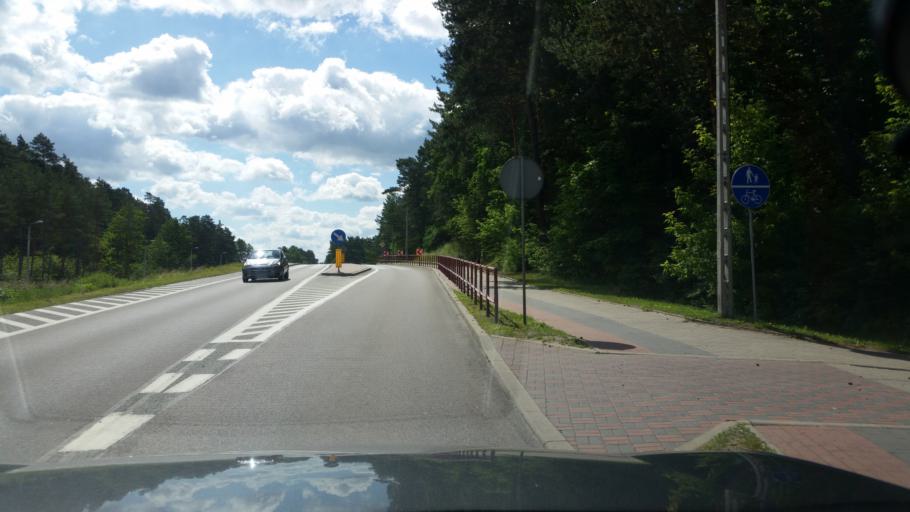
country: PL
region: Podlasie
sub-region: Powiat augustowski
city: Augustow
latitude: 53.8635
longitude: 23.0017
